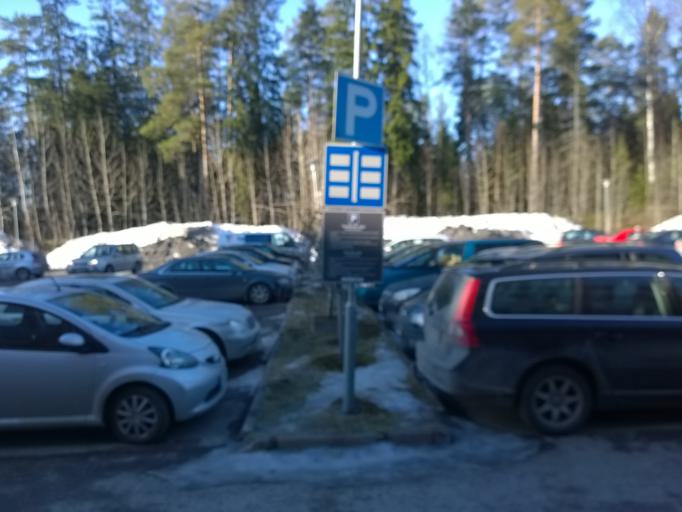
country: FI
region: Pirkanmaa
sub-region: Tampere
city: Tampere
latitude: 61.4476
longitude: 23.8578
